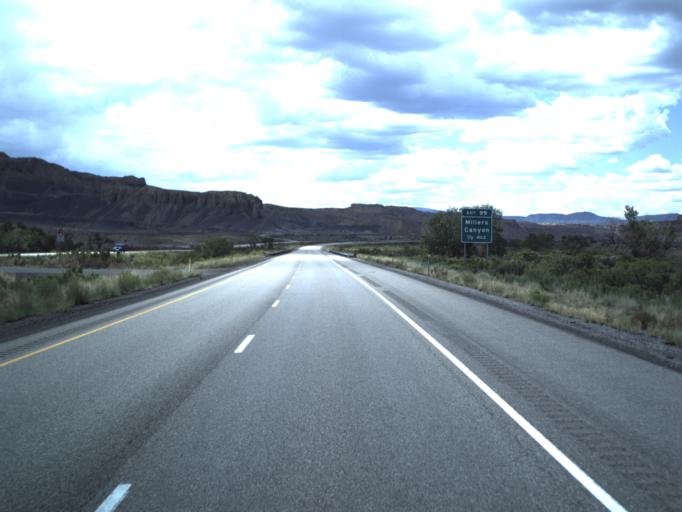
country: US
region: Utah
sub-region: Emery County
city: Ferron
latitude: 38.8144
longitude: -111.1971
